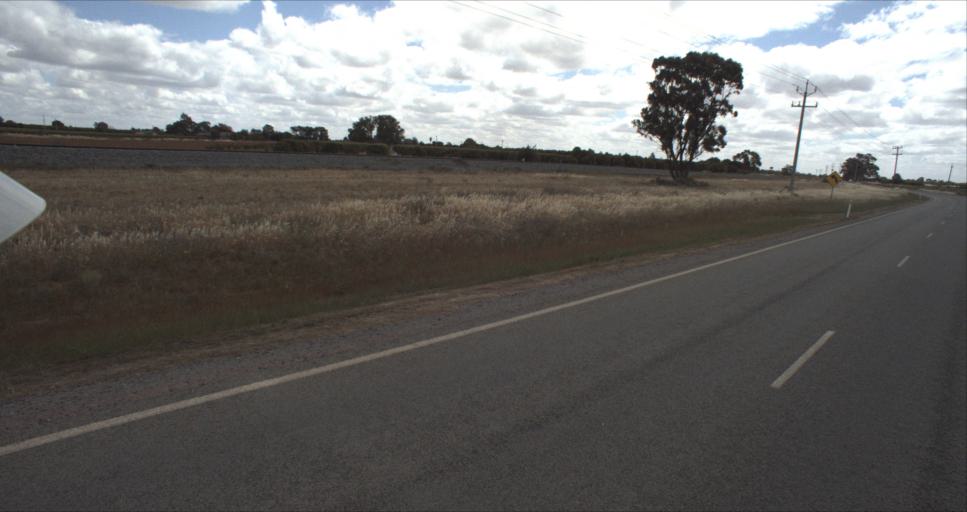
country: AU
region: New South Wales
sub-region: Leeton
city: Leeton
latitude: -34.5821
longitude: 146.4012
